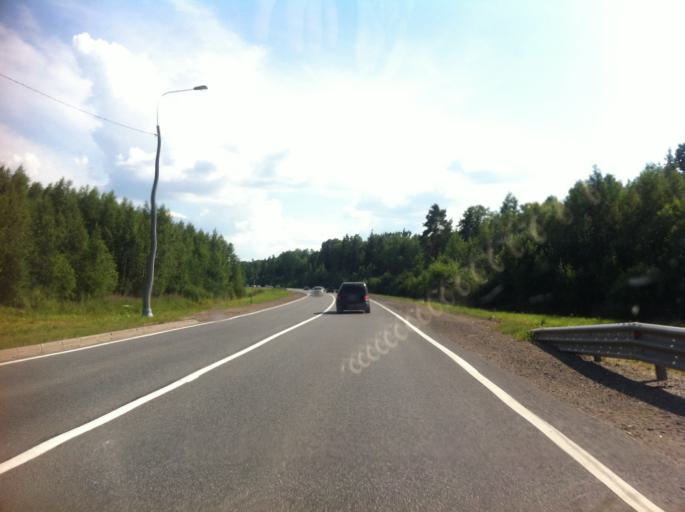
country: RU
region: Leningrad
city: Tolmachevo
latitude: 58.9188
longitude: 29.9625
